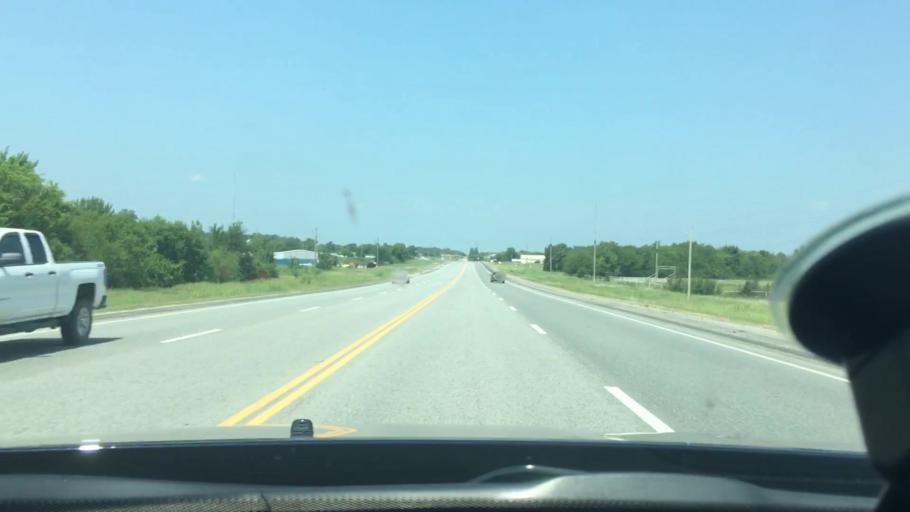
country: US
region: Oklahoma
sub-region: Atoka County
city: Atoka
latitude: 34.3645
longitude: -96.1006
